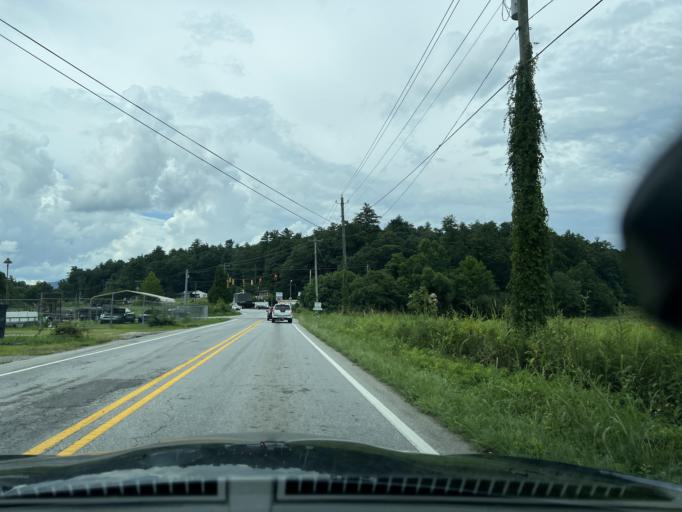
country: US
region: North Carolina
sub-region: Henderson County
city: Hoopers Creek
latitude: 35.4523
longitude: -82.4779
